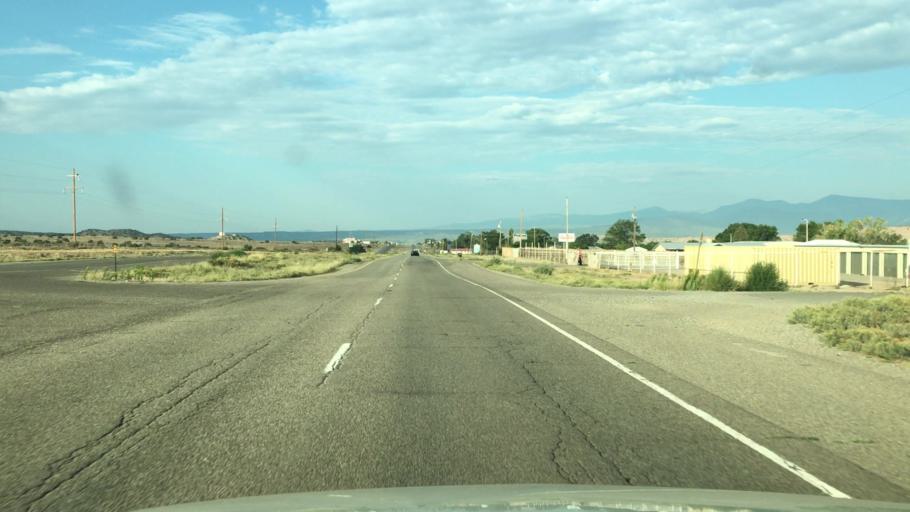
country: US
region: New Mexico
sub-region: Rio Arriba County
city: Ohkay Owingeh
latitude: 36.1158
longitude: -106.0206
